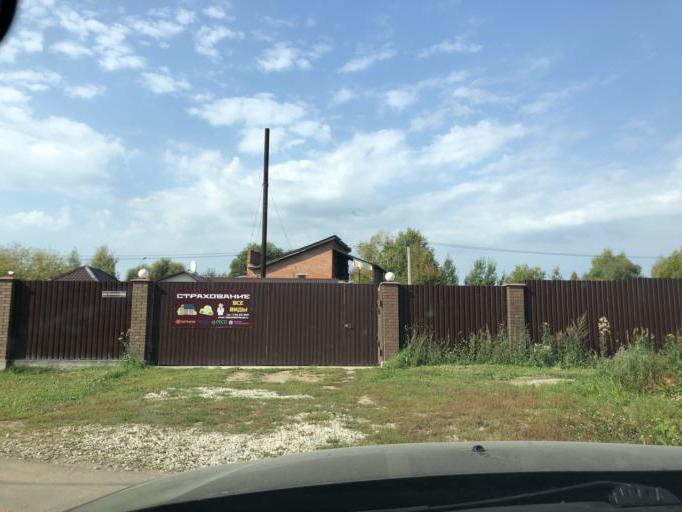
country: RU
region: Moskovskaya
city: L'vovskiy
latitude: 55.3442
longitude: 37.4495
